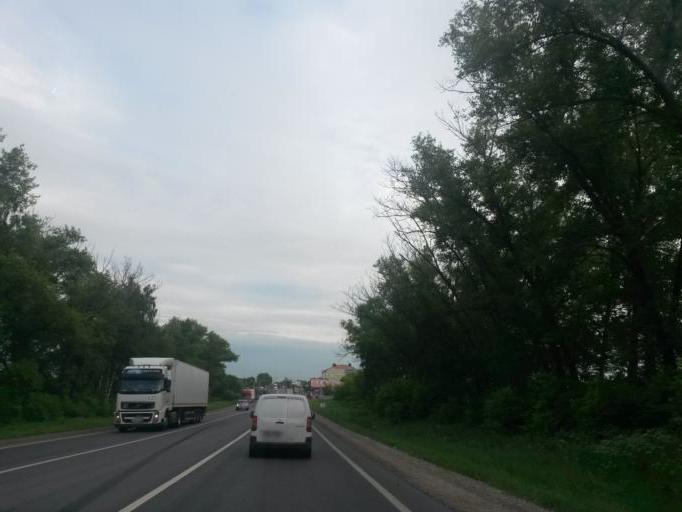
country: RU
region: Moskovskaya
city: Belyye Stolby
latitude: 55.3172
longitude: 37.8099
